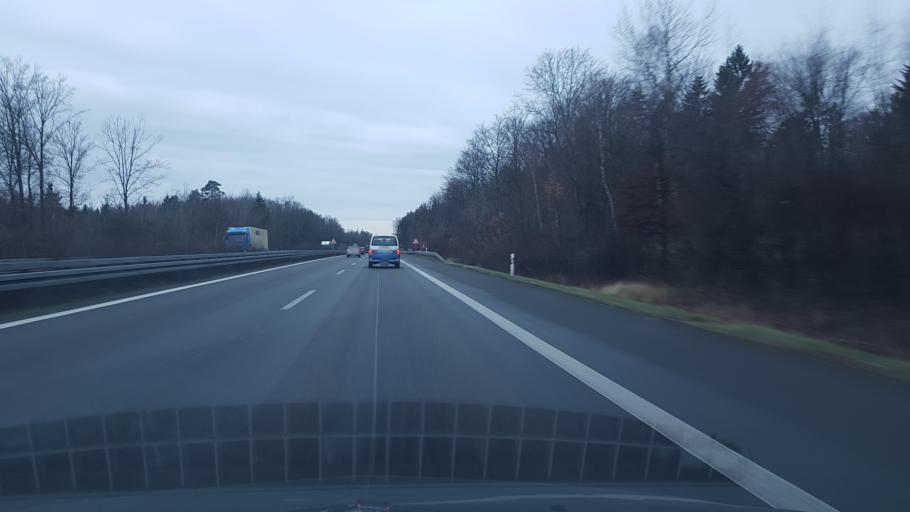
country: DE
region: Saxony
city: Grossrohrsdorf
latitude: 51.1552
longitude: 14.0043
